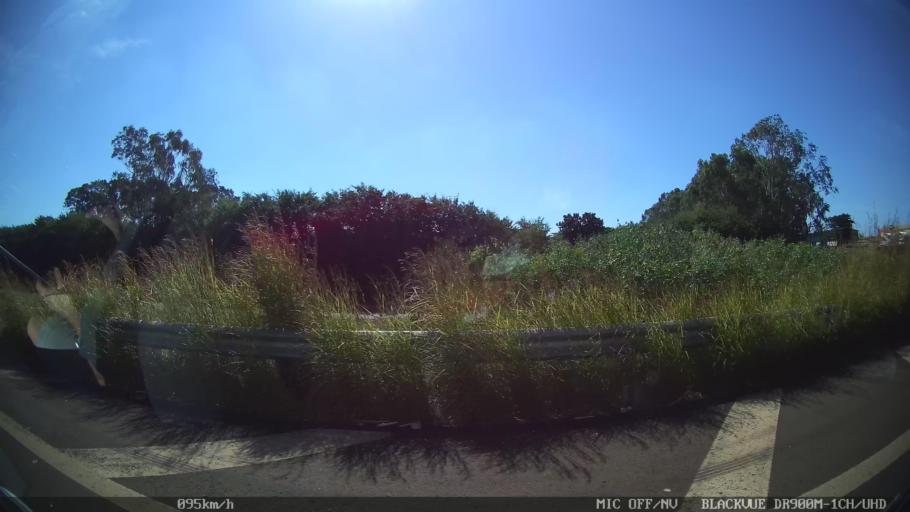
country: BR
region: Sao Paulo
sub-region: Franca
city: Franca
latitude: -20.5472
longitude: -47.4602
